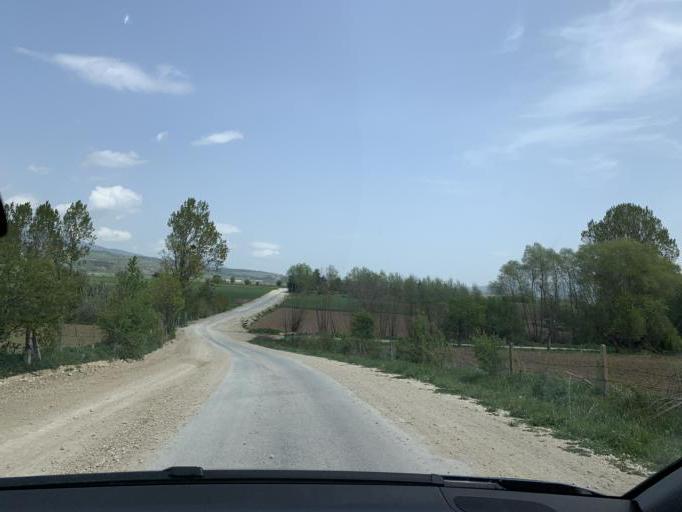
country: TR
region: Bolu
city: Bolu
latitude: 40.7533
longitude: 31.6742
